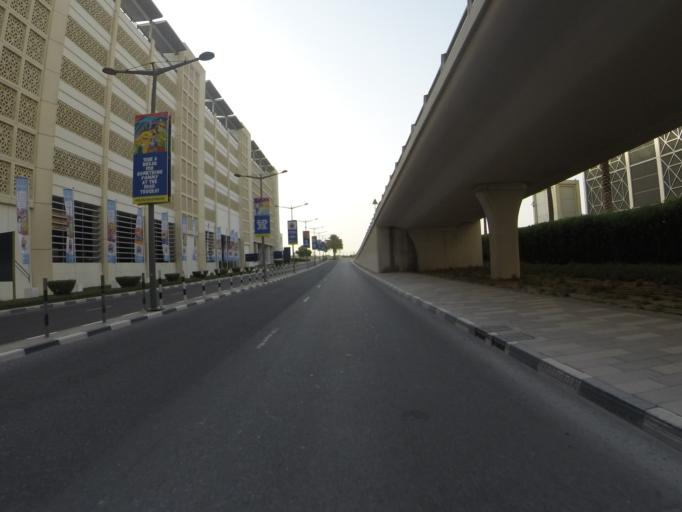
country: AE
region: Ash Shariqah
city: Sharjah
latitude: 25.2217
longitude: 55.2864
